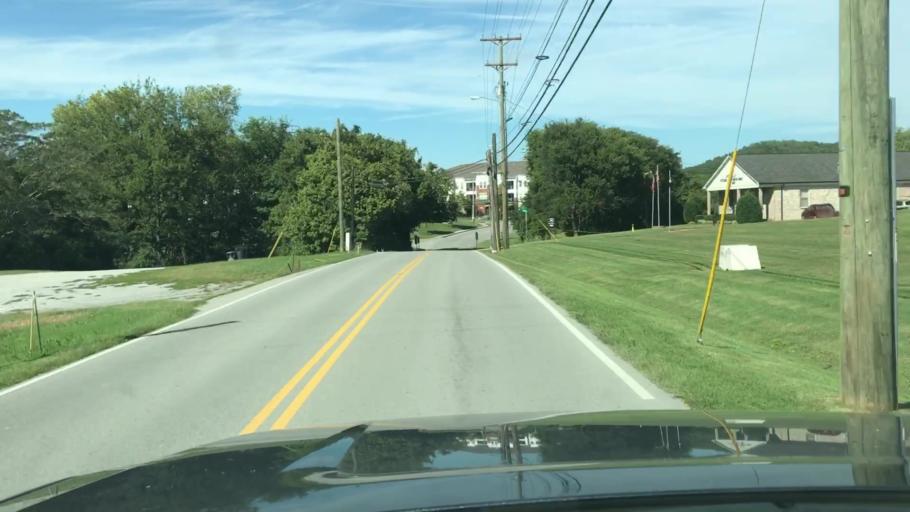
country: US
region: Tennessee
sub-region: Williamson County
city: Franklin
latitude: 35.9279
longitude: -86.8564
